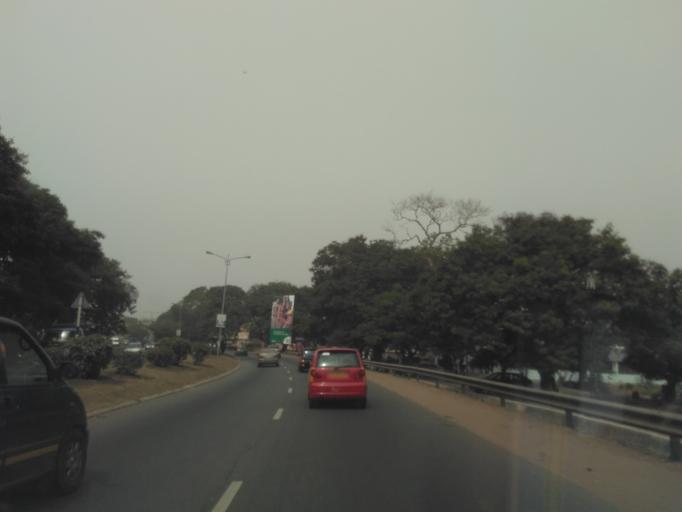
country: GH
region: Greater Accra
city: Accra
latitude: 5.5743
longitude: -0.1942
